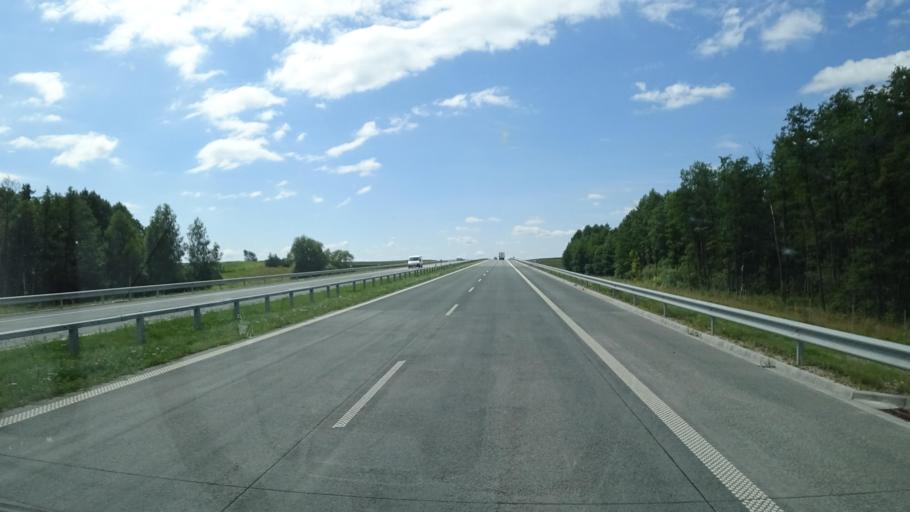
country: PL
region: Podlasie
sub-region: Powiat grajewski
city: Szczuczyn
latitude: 53.5129
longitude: 22.2483
